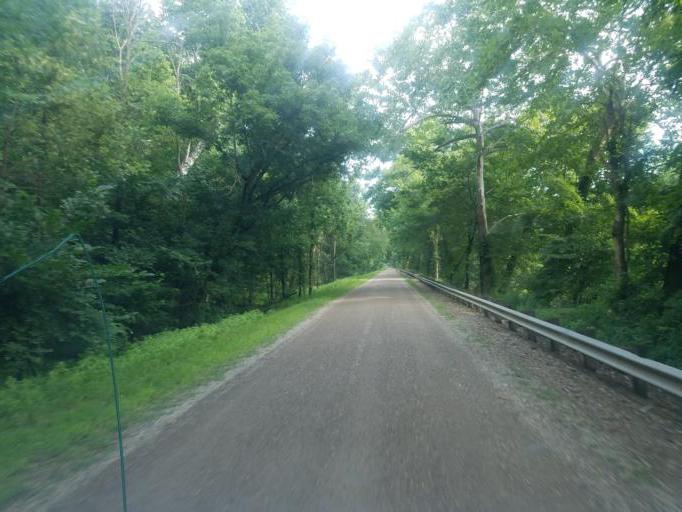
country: US
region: Ohio
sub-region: Knox County
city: Oak Hill
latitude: 40.3950
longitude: -82.1594
